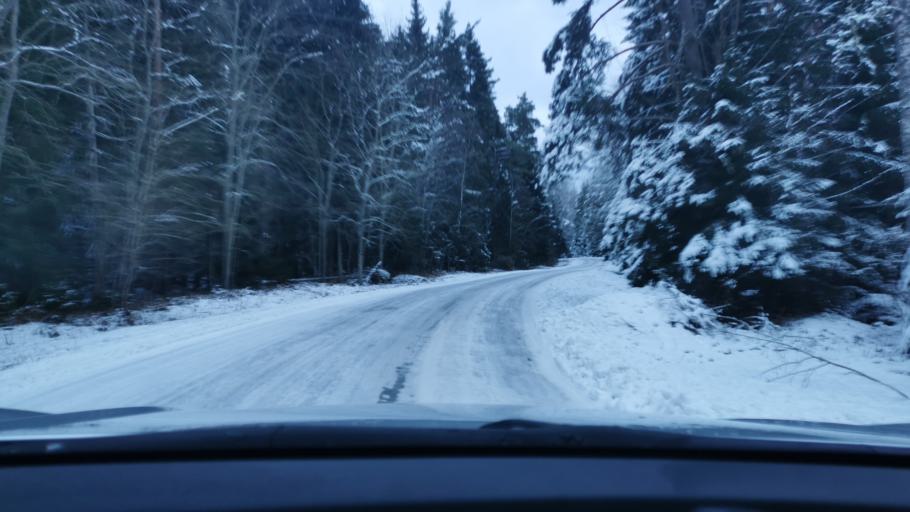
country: EE
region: Laeaene-Virumaa
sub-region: Haljala vald
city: Haljala
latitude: 59.5601
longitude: 26.3142
